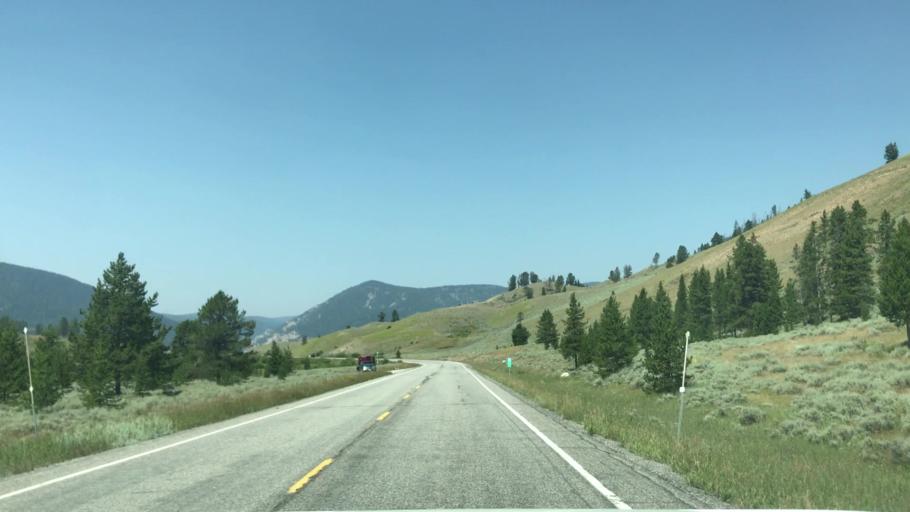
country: US
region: Montana
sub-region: Gallatin County
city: Big Sky
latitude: 45.0371
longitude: -111.1173
